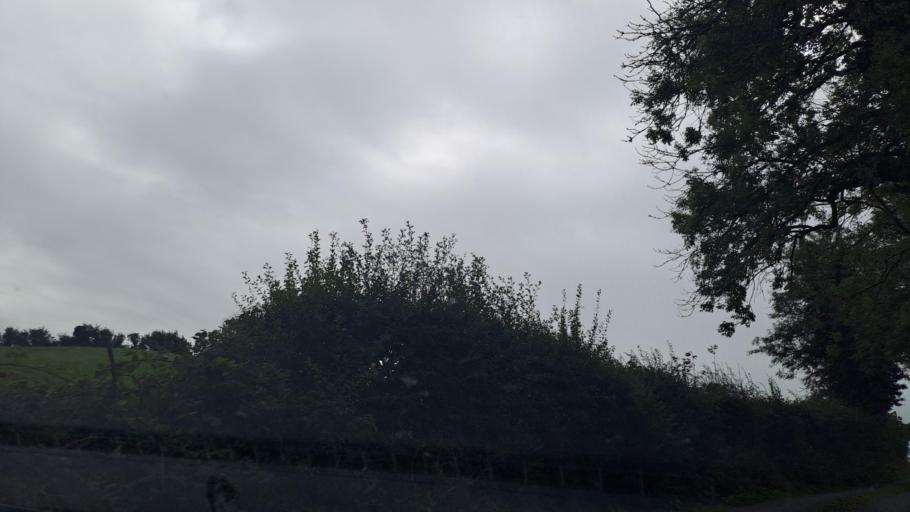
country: IE
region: Ulster
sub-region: An Cabhan
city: Kingscourt
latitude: 53.9883
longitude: -6.8315
